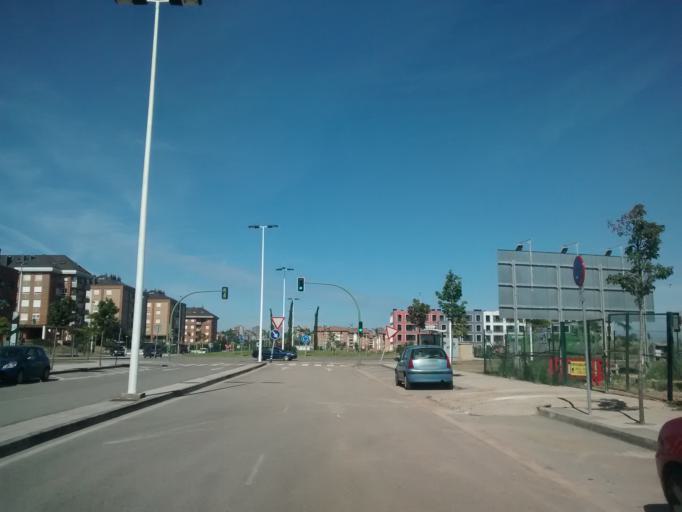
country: ES
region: Cantabria
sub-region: Provincia de Cantabria
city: Camargo
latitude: 43.4409
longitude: -3.8516
